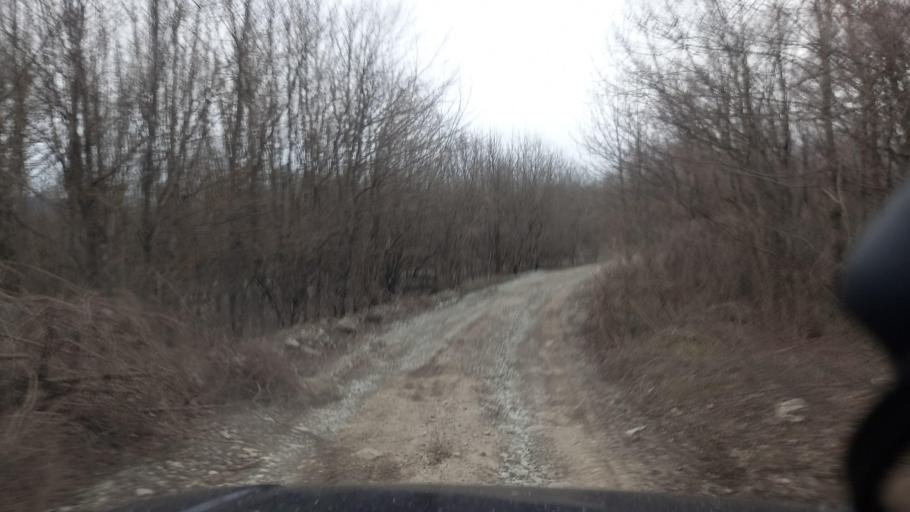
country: RU
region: Krasnodarskiy
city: Pshada
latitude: 44.5939
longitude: 38.2985
